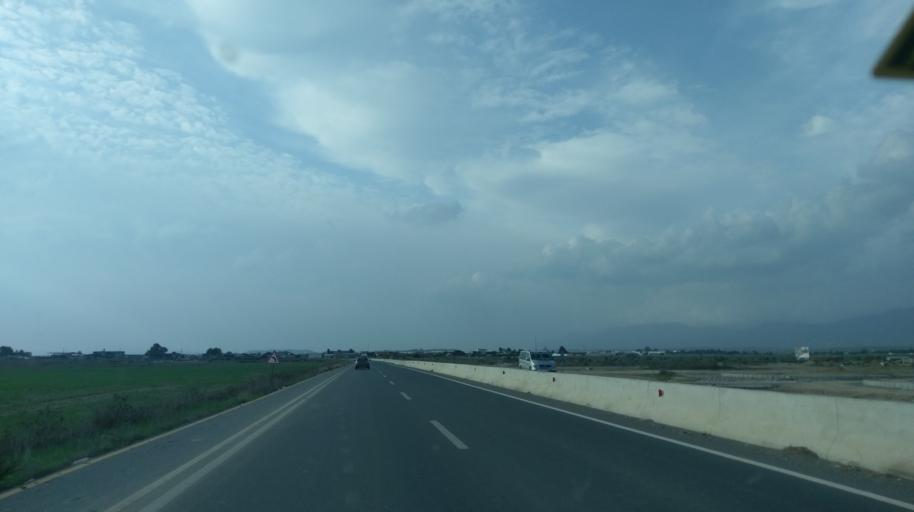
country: CY
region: Lefkosia
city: Nicosia
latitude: 35.1997
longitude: 33.2893
